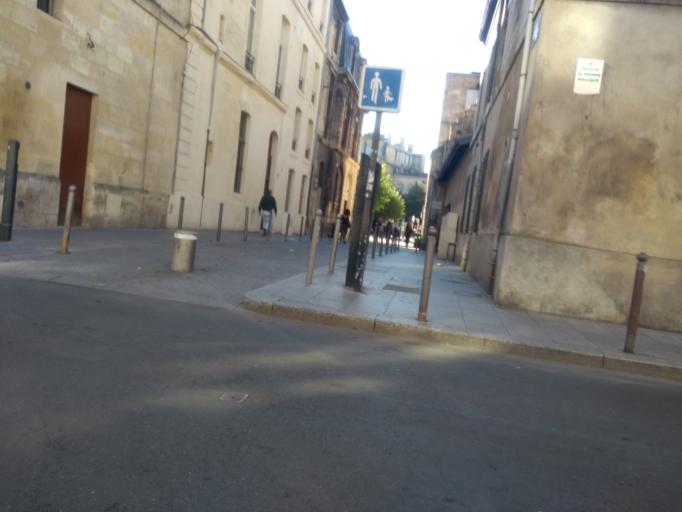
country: FR
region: Aquitaine
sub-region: Departement de la Gironde
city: Bordeaux
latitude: 44.8315
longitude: -0.5720
